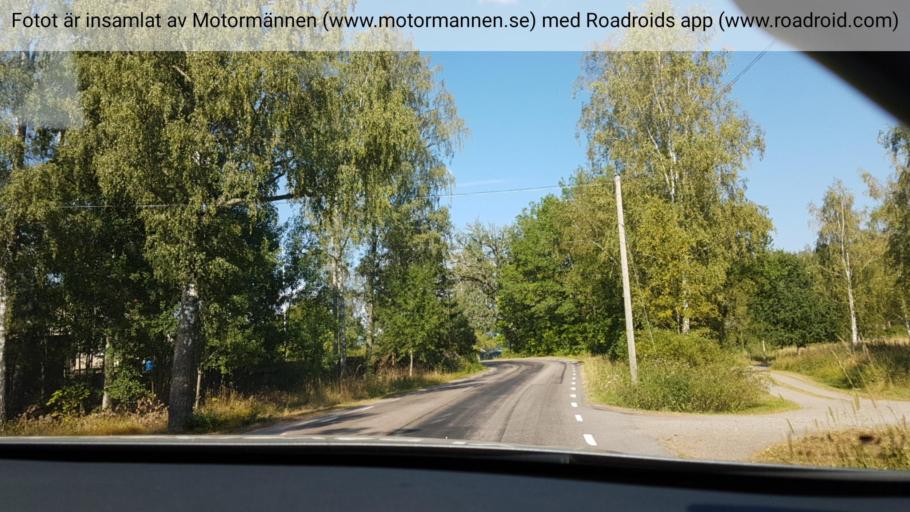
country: SE
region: Vaestra Goetaland
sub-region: Mariestads Kommun
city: Mariestad
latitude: 58.6187
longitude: 13.8802
